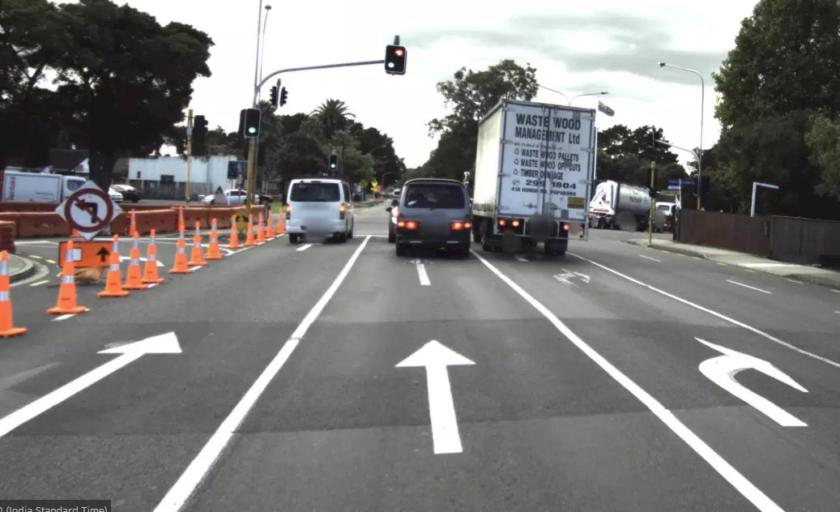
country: NZ
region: Auckland
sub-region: Auckland
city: Papakura
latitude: -37.0723
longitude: 174.9429
